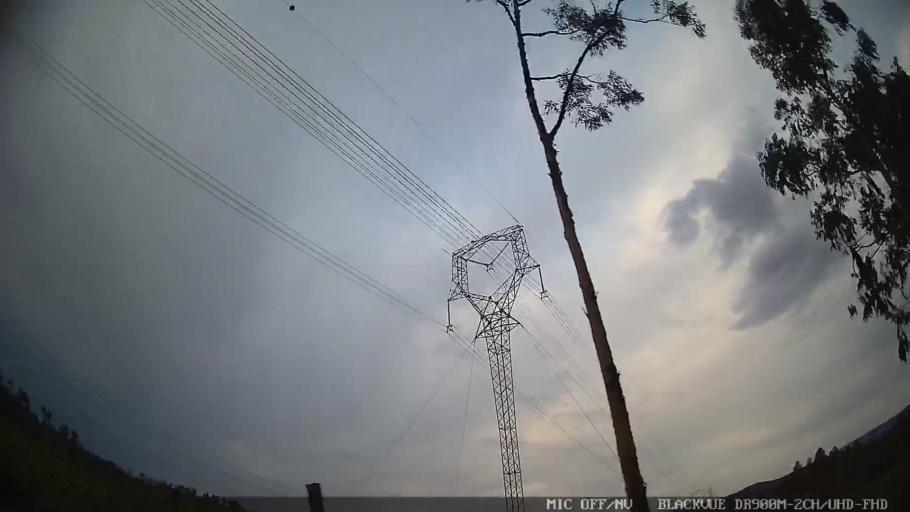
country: BR
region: Sao Paulo
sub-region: Itatiba
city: Itatiba
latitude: -23.0175
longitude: -46.9067
